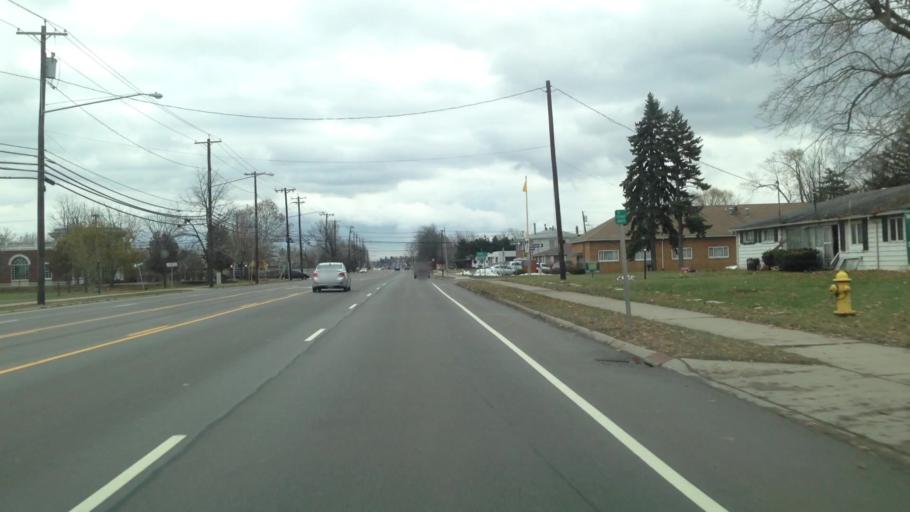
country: US
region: New York
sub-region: Erie County
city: Williamsville
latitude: 42.9658
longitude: -78.7102
